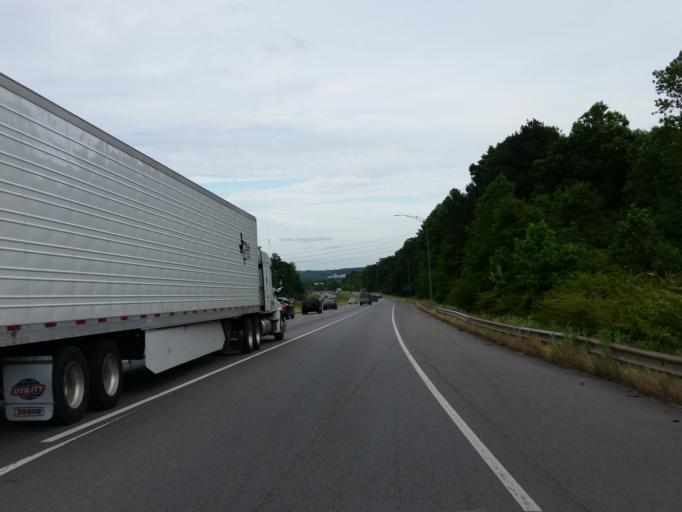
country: US
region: Alabama
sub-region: Tuscaloosa County
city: Holt
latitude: 33.1734
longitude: -87.4715
